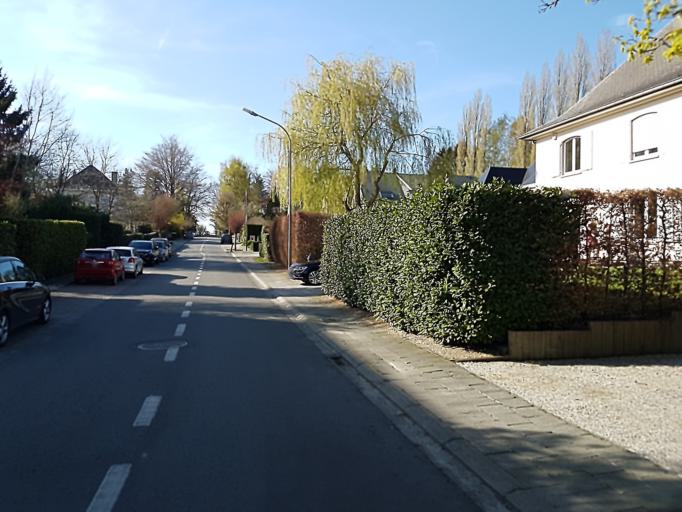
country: BE
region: Flanders
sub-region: Provincie Vlaams-Brabant
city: Sint-Genesius-Rode
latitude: 50.7556
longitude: 4.3755
